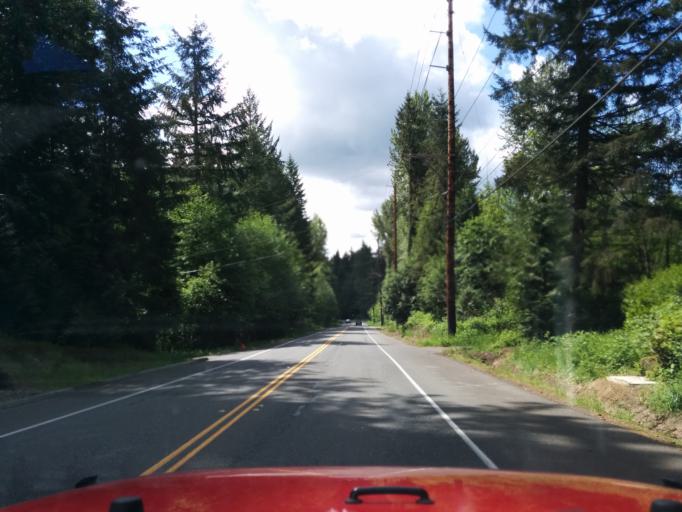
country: US
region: Washington
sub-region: King County
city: Union Hill-Novelty Hill
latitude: 47.6703
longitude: -122.0221
